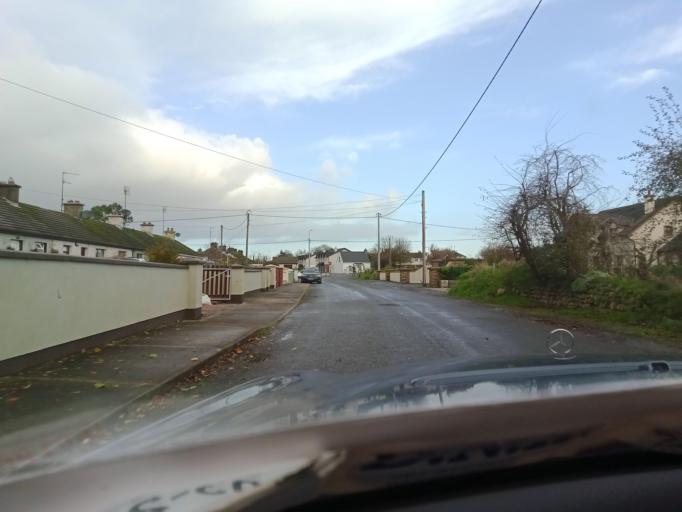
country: IE
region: Leinster
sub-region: Kilkenny
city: Mooncoin
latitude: 52.2904
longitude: -7.2519
